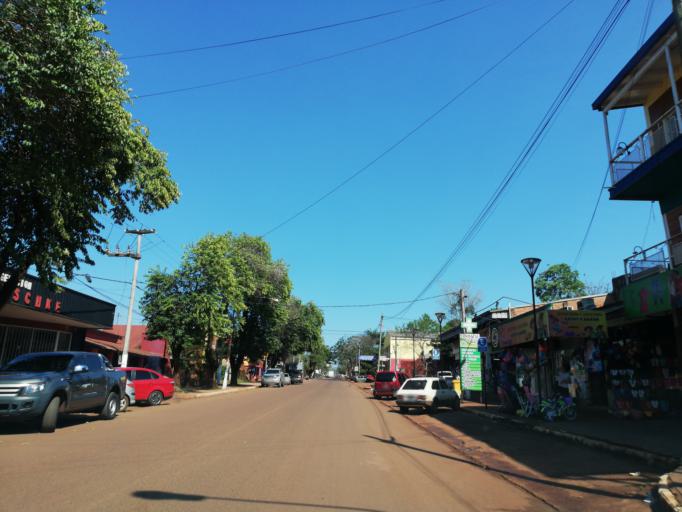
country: AR
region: Misiones
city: Puerto Eldorado
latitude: -26.4069
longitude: -54.6630
